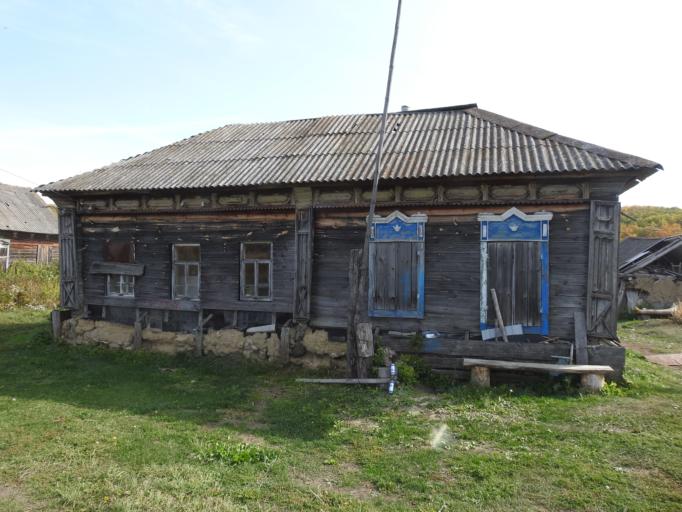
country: RU
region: Saratov
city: Baltay
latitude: 52.5170
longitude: 46.6826
